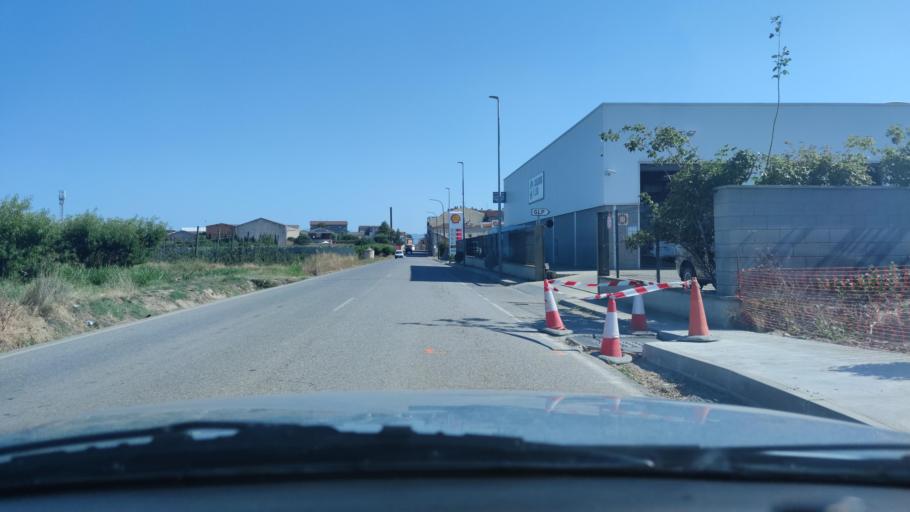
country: ES
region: Catalonia
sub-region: Provincia de Lleida
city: Bellvis
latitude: 41.6693
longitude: 0.8140
